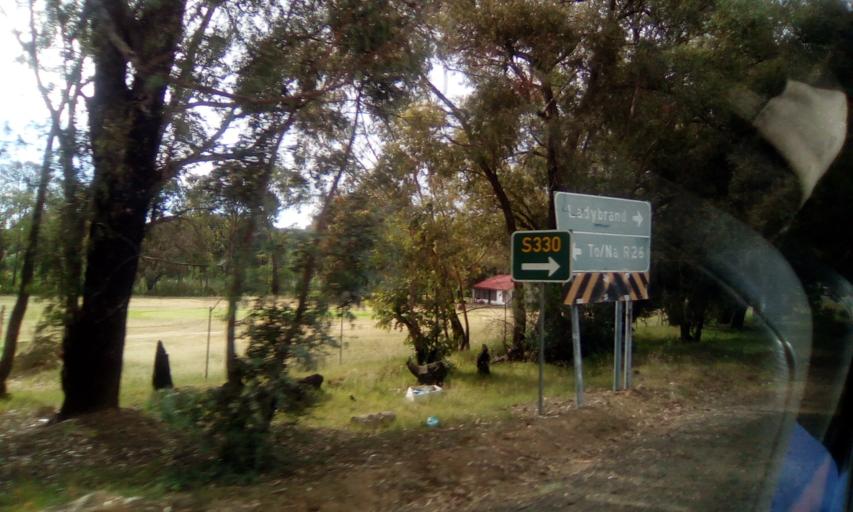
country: ZA
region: Orange Free State
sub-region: Thabo Mofutsanyana District Municipality
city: Ladybrand
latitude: -29.2016
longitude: 27.4653
